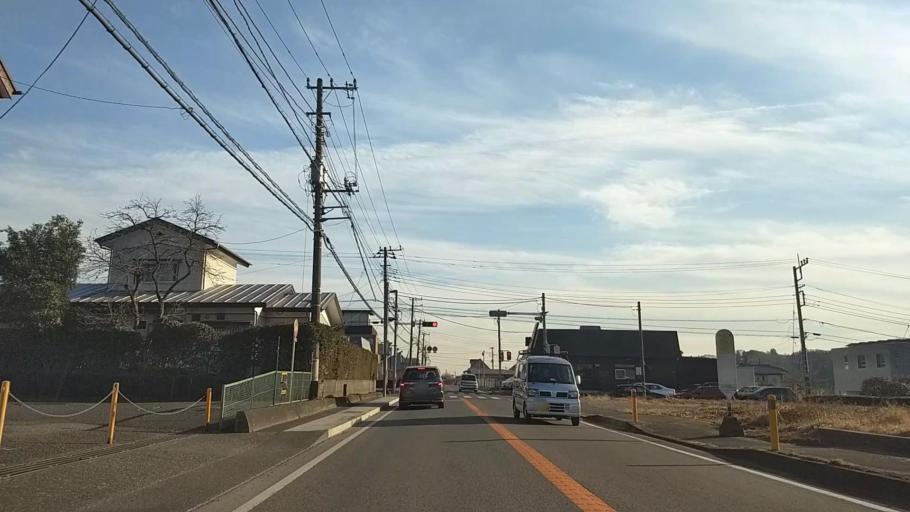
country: JP
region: Kanagawa
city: Zama
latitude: 35.5051
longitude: 139.3097
